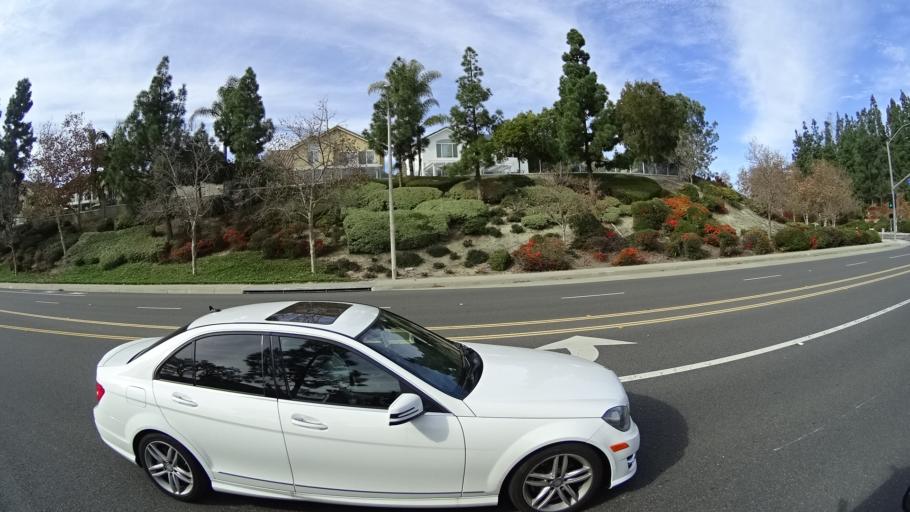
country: US
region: California
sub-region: Orange County
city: Aliso Viejo
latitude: 33.5811
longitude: -117.7392
